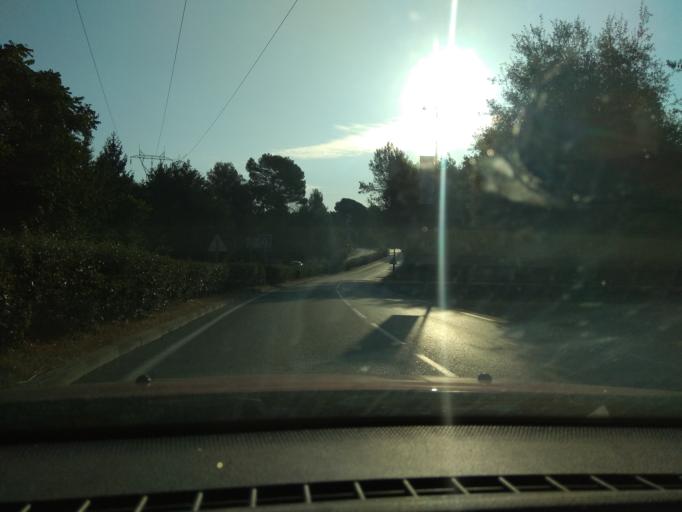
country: FR
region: Provence-Alpes-Cote d'Azur
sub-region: Departement des Alpes-Maritimes
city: Le Rouret
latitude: 43.6440
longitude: 7.0466
